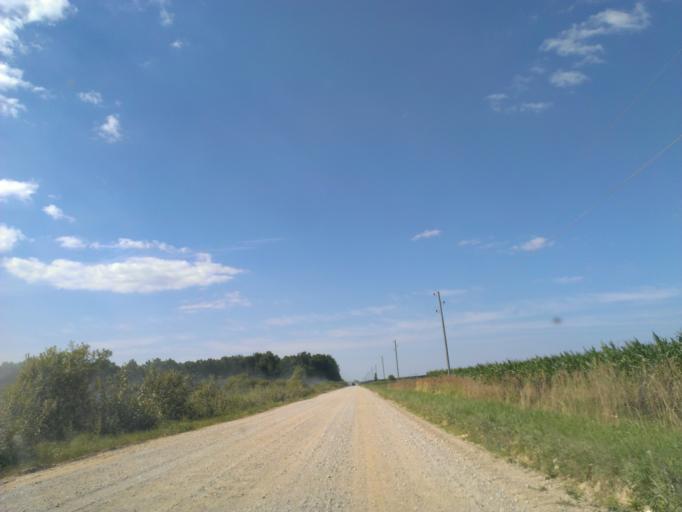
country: LV
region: Carnikava
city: Carnikava
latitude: 57.0778
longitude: 24.2675
